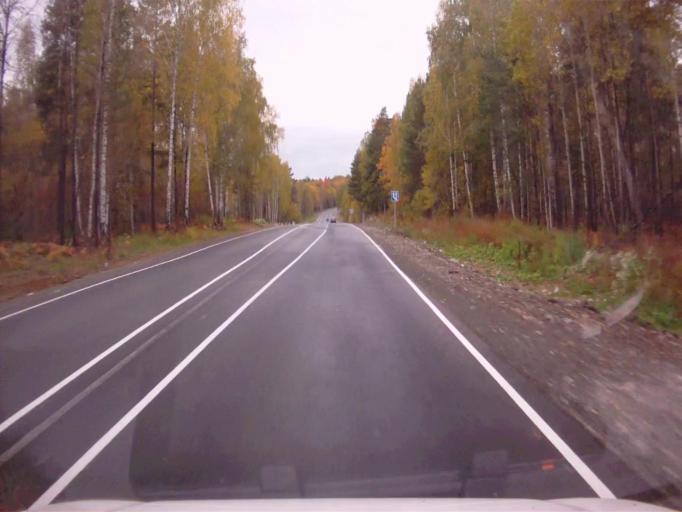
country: RU
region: Chelyabinsk
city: Nyazepetrovsk
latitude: 56.0673
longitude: 59.6959
